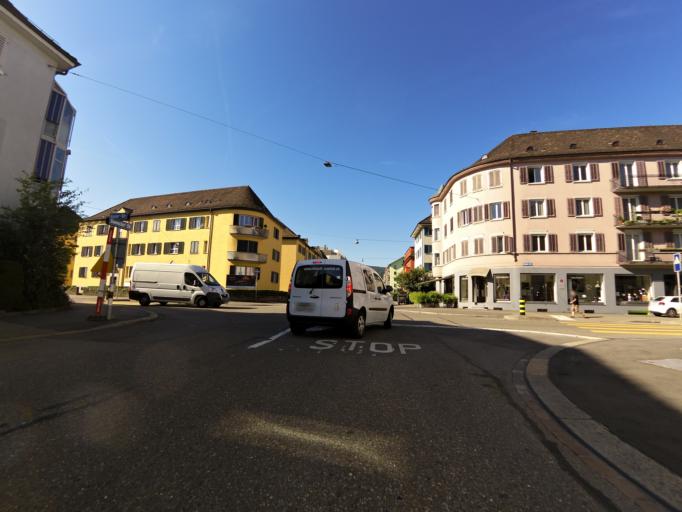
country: CH
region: Zurich
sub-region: Bezirk Zuerich
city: Zuerich (Kreis 9) / Altstetten
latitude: 47.3892
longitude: 8.4890
